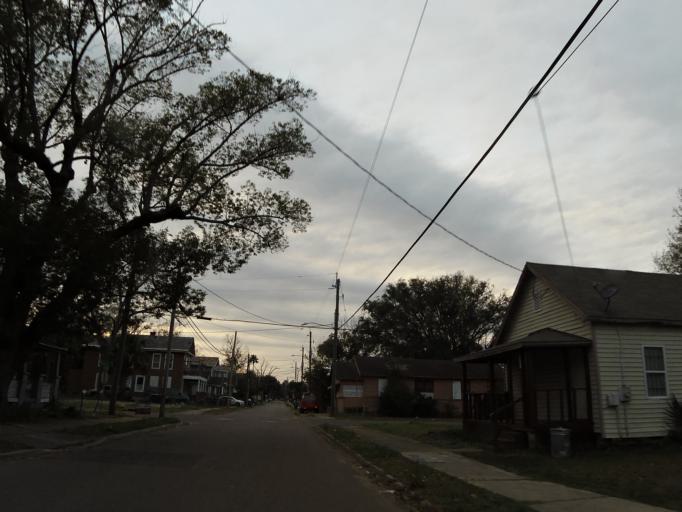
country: US
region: Florida
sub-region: Duval County
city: Jacksonville
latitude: 30.3428
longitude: -81.6736
